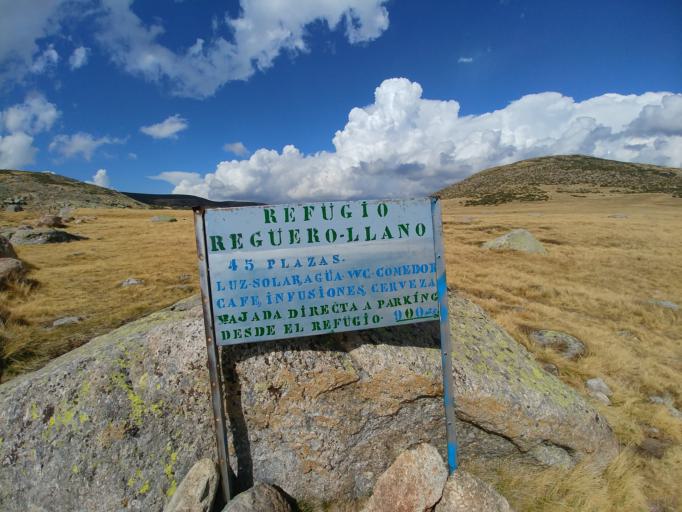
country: ES
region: Castille and Leon
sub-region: Provincia de Avila
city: Hoyos del Collado
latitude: 40.2708
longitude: -5.2401
